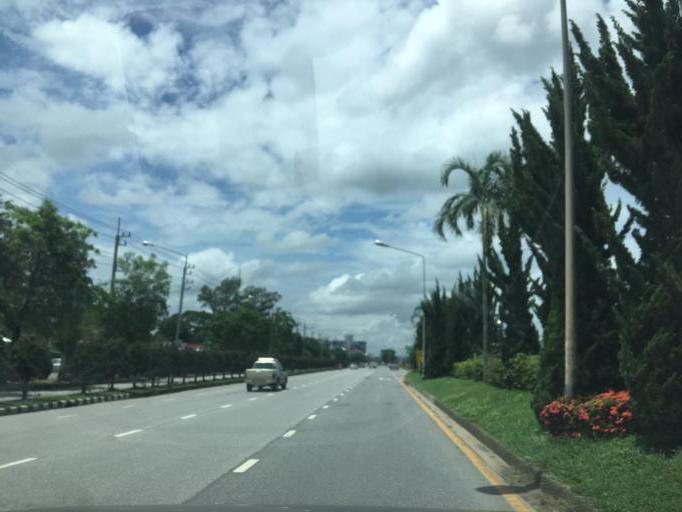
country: TH
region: Chiang Rai
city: Chiang Rai
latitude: 19.8891
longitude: 99.8362
